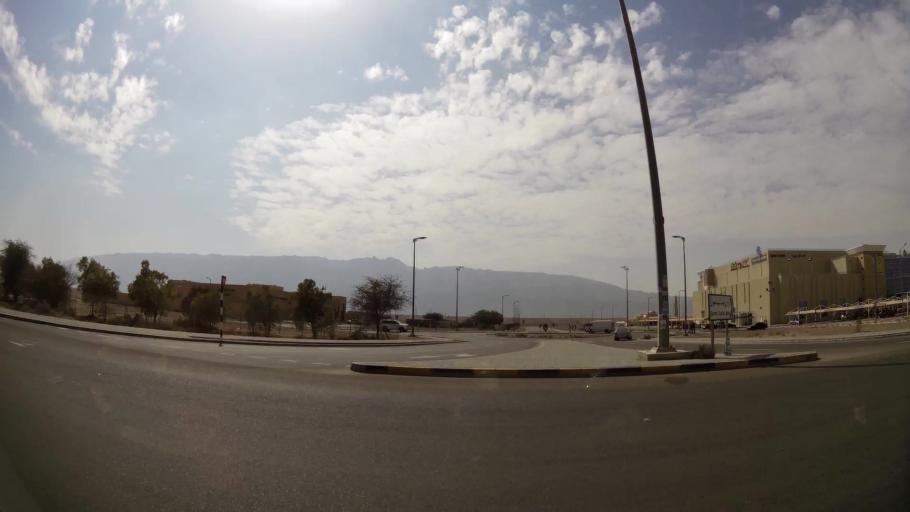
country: AE
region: Abu Dhabi
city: Al Ain
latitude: 24.0854
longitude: 55.8317
